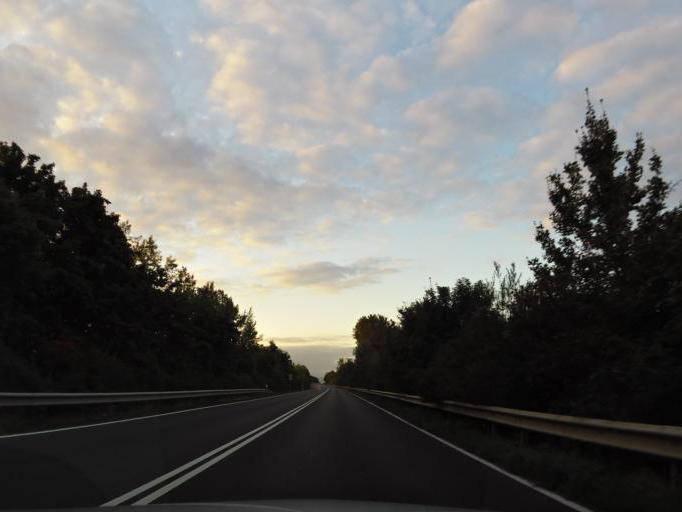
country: DE
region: Rheinland-Pfalz
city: Nackenheim
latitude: 49.9217
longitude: 8.3460
